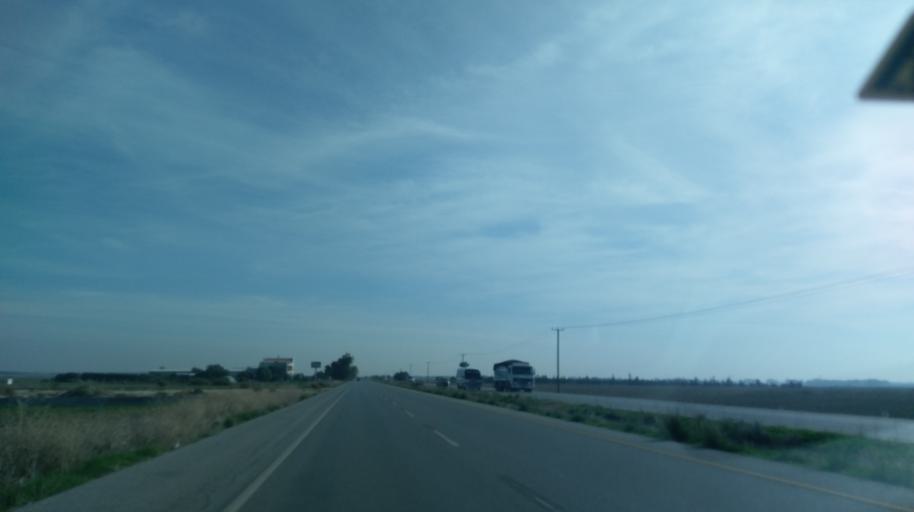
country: CY
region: Larnaka
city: Athienou
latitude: 35.2113
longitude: 33.5478
